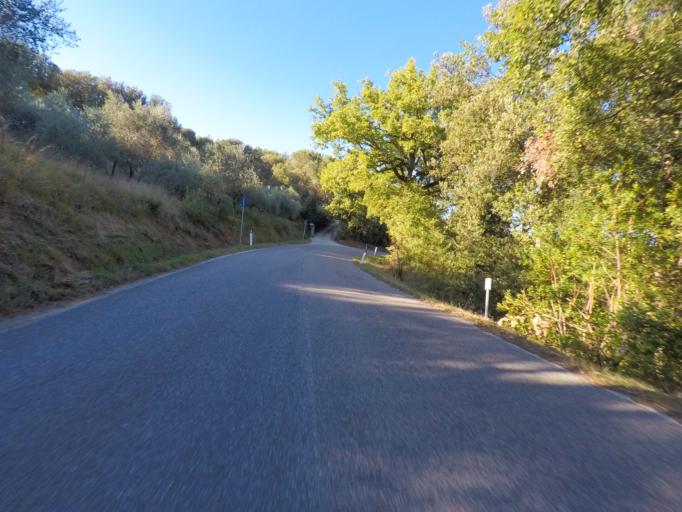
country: IT
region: Tuscany
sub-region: Provincia di Siena
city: Belverde
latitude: 43.4083
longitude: 11.3516
